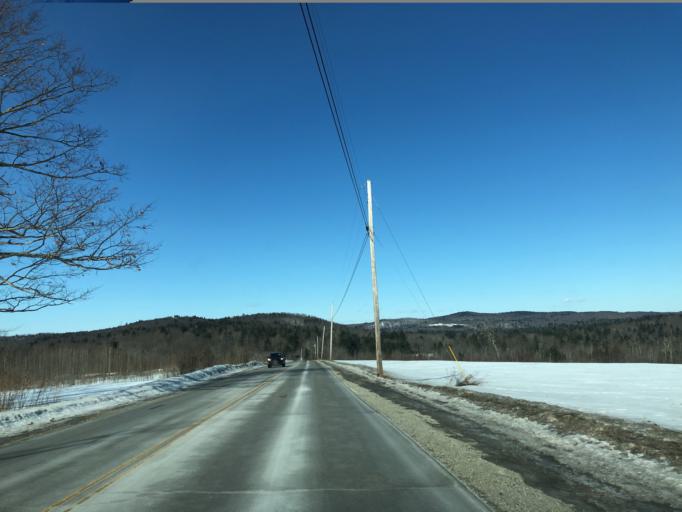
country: US
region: Maine
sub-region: Androscoggin County
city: Minot
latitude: 44.1372
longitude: -70.3178
